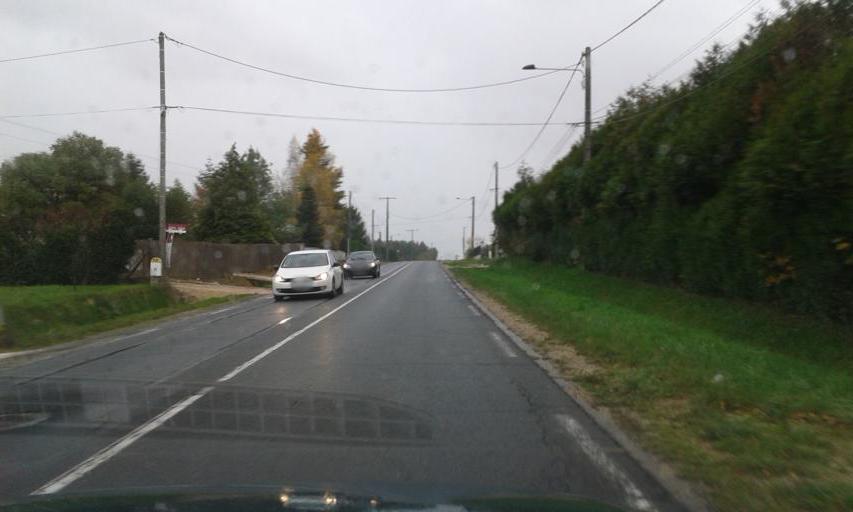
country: FR
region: Centre
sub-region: Departement du Loiret
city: Fay-aux-Loges
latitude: 47.9187
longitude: 2.1356
